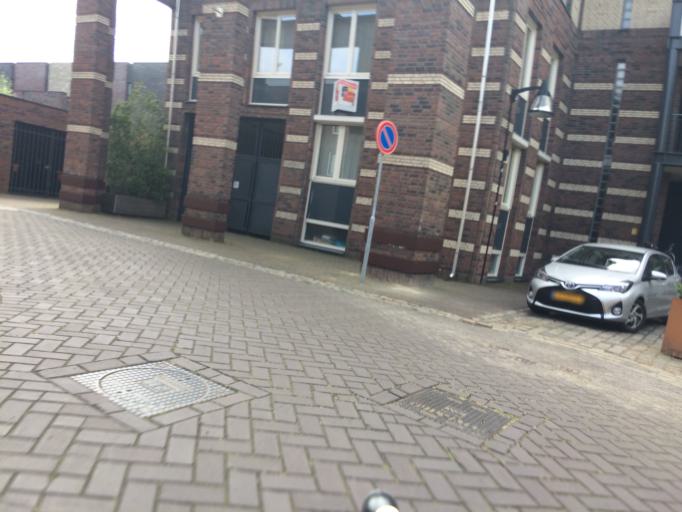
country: NL
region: Gelderland
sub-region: Gemeente Maasdriel
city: Hedel
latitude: 51.7275
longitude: 5.2556
